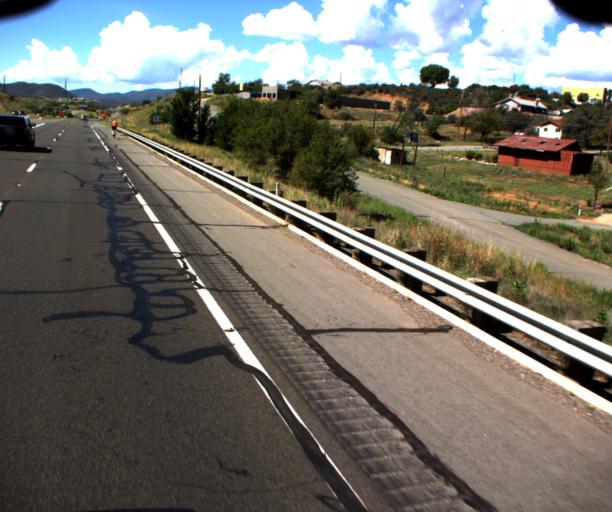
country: US
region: Arizona
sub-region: Yavapai County
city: Dewey-Humboldt
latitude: 34.5074
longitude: -112.2423
